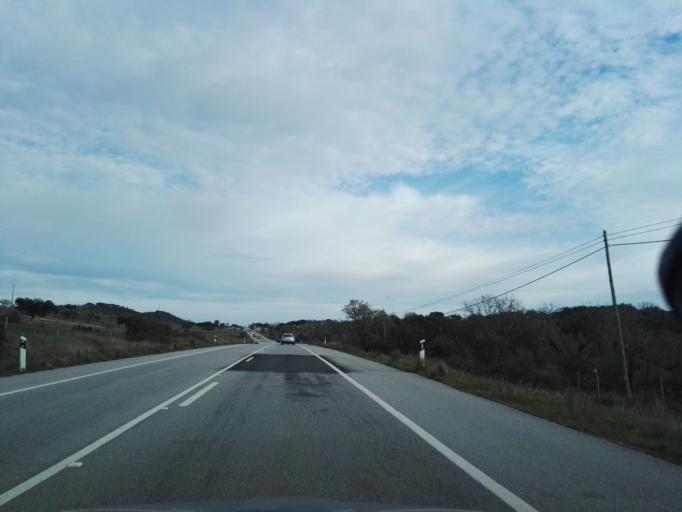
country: PT
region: Portalegre
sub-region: Portalegre
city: Urra
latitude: 39.2483
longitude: -7.4026
